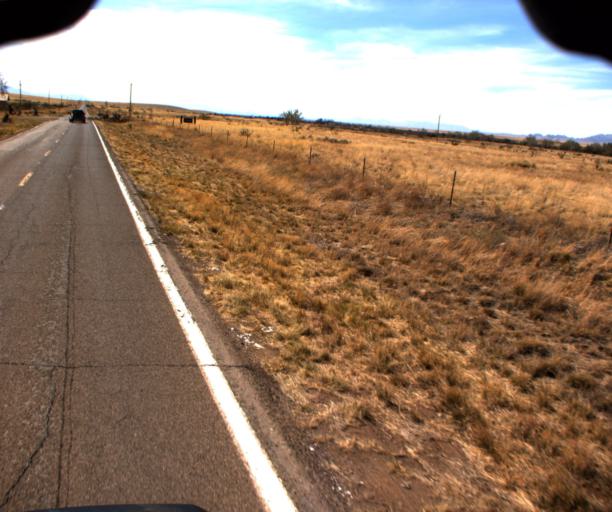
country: US
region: Arizona
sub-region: Cochise County
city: Willcox
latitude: 32.0067
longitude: -109.4040
